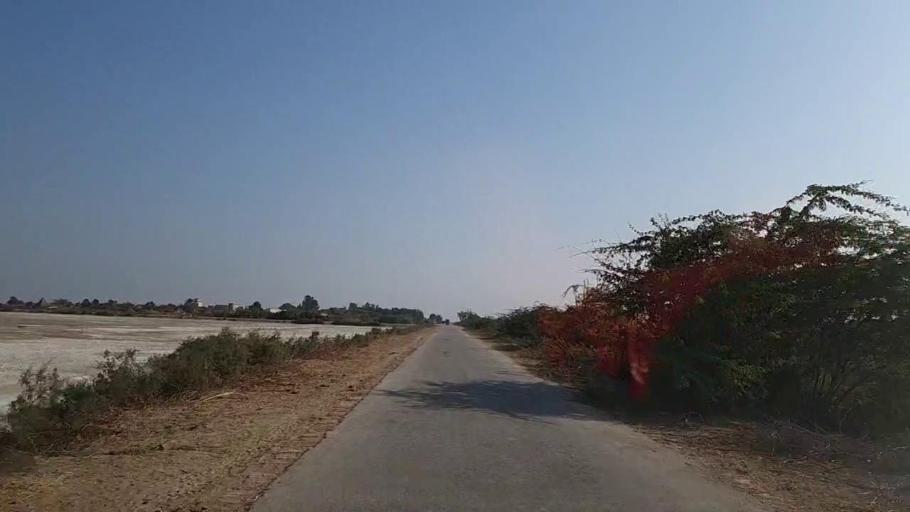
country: PK
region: Sindh
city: Tando Mittha Khan
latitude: 25.9310
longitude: 69.0624
